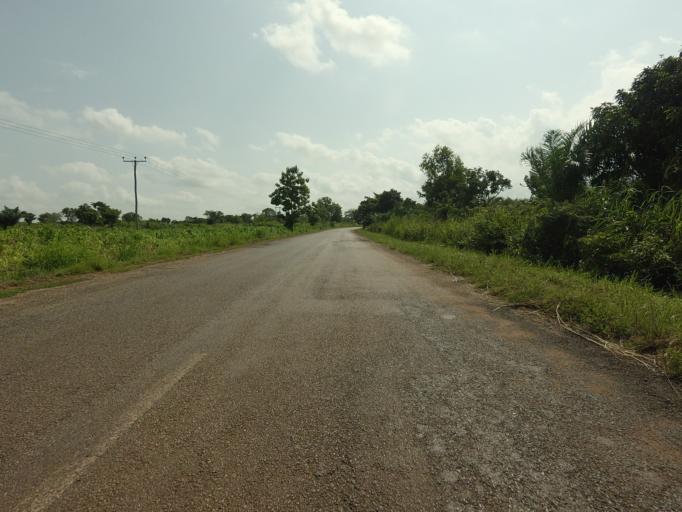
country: GH
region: Volta
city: Ho
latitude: 6.3936
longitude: 0.8015
